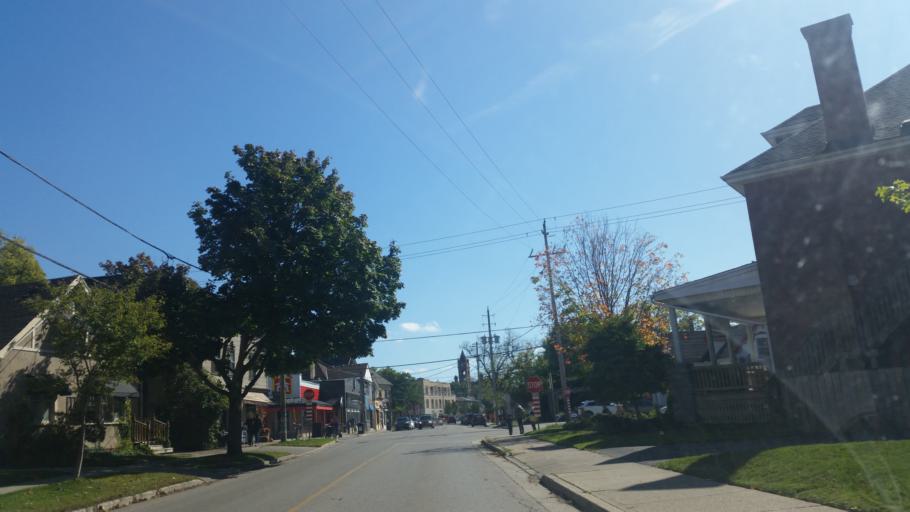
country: CA
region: Ontario
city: London
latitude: 42.9738
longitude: -81.2546
